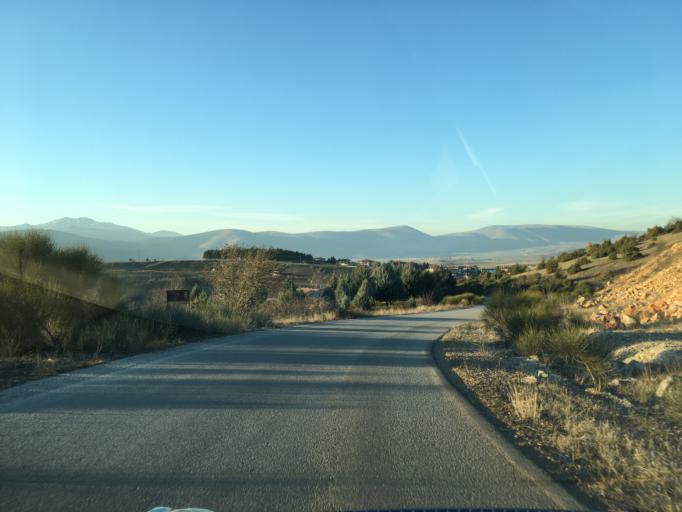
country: GR
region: West Macedonia
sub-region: Nomos Kozanis
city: Kozani
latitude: 40.2800
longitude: 21.7333
